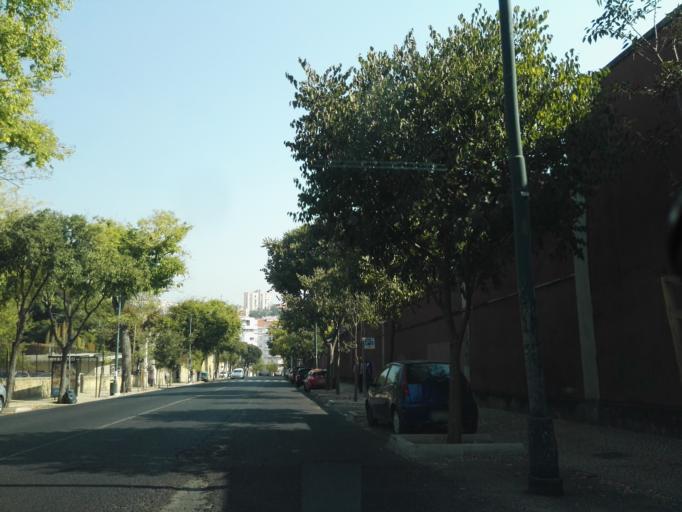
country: PT
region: Lisbon
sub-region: Lisbon
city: Lisbon
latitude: 38.7275
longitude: -9.1402
